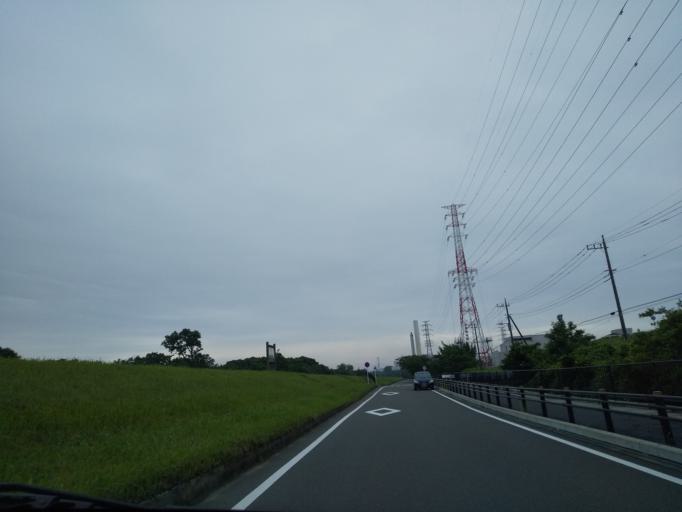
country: JP
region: Tokyo
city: Hino
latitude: 35.6720
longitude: 139.4254
